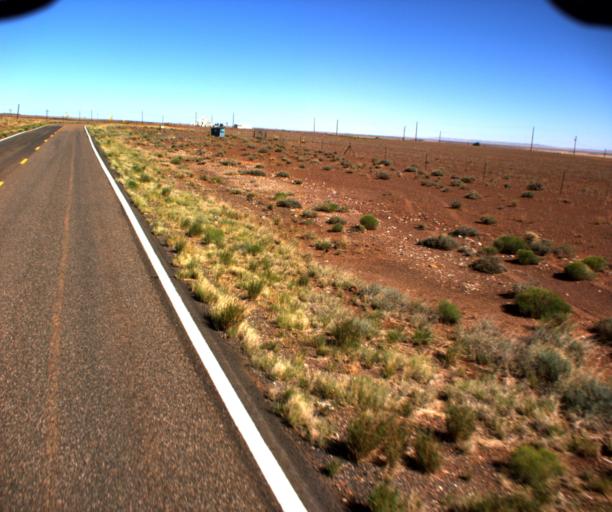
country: US
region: Arizona
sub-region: Coconino County
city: LeChee
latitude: 35.1359
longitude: -110.8865
